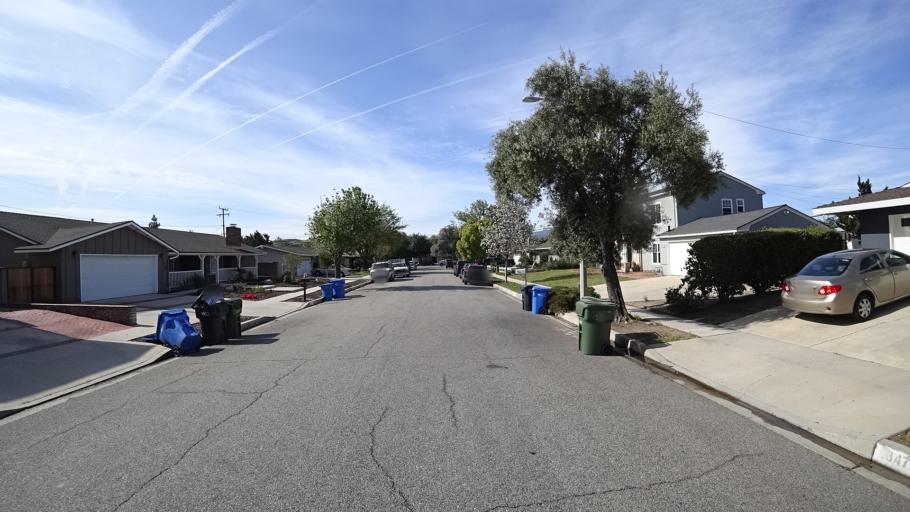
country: US
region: California
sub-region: Ventura County
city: Thousand Oaks
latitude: 34.1975
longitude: -118.8805
